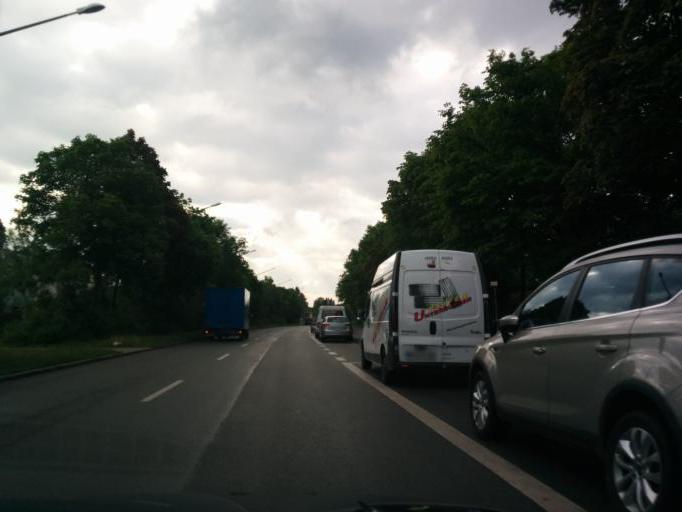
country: DE
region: Bavaria
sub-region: Upper Bavaria
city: Bogenhausen
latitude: 48.1176
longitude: 11.6368
